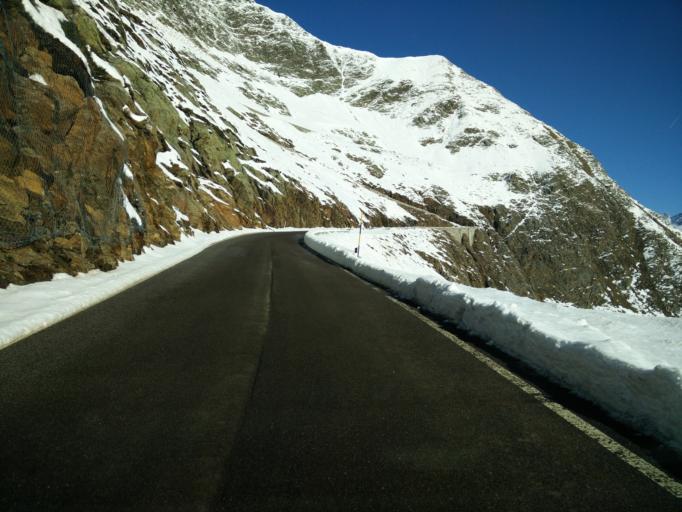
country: IT
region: Trentino-Alto Adige
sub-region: Bolzano
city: Moso in Passiria
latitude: 46.8859
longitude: 11.1112
